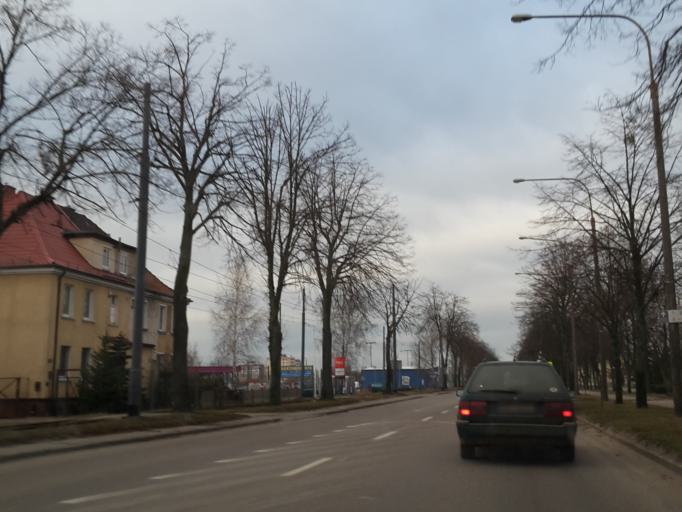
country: PL
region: Warmian-Masurian Voivodeship
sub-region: Powiat elblaski
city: Elblag
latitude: 54.1474
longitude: 19.4325
